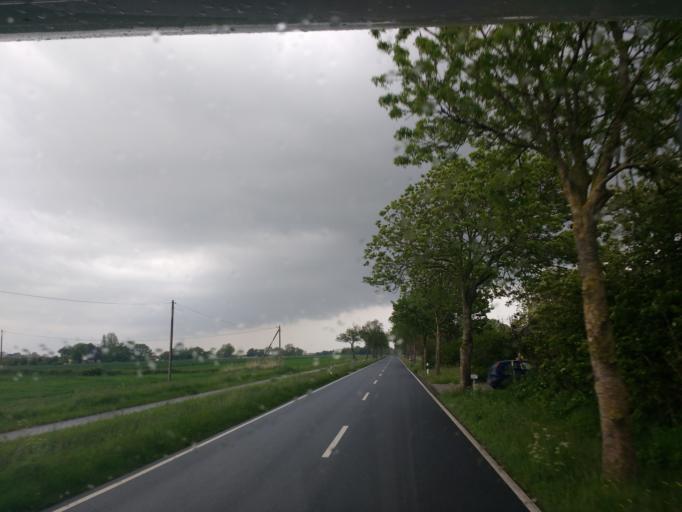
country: DE
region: Lower Saxony
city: Wangerooge
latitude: 53.6989
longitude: 7.9147
